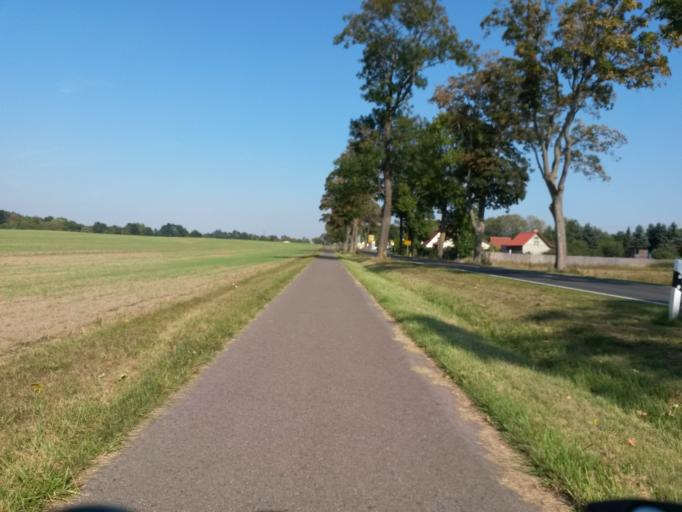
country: DE
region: Brandenburg
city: Templin
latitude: 53.1015
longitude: 13.4727
